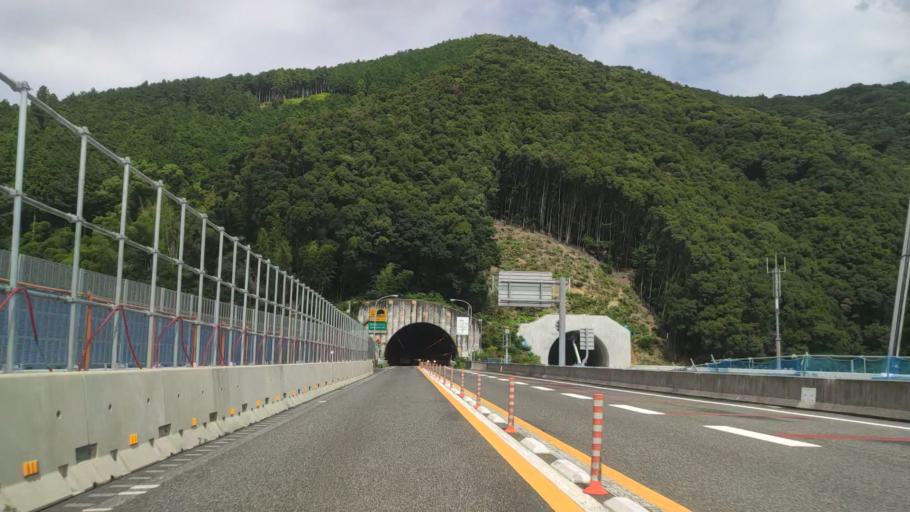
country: JP
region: Wakayama
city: Gobo
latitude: 33.9709
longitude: 135.1975
